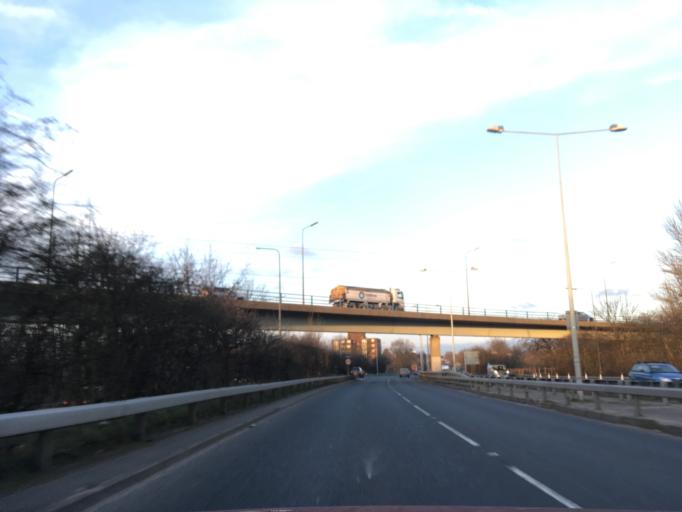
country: GB
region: England
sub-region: Manchester
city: Didsbury
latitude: 53.3991
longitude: -2.2263
